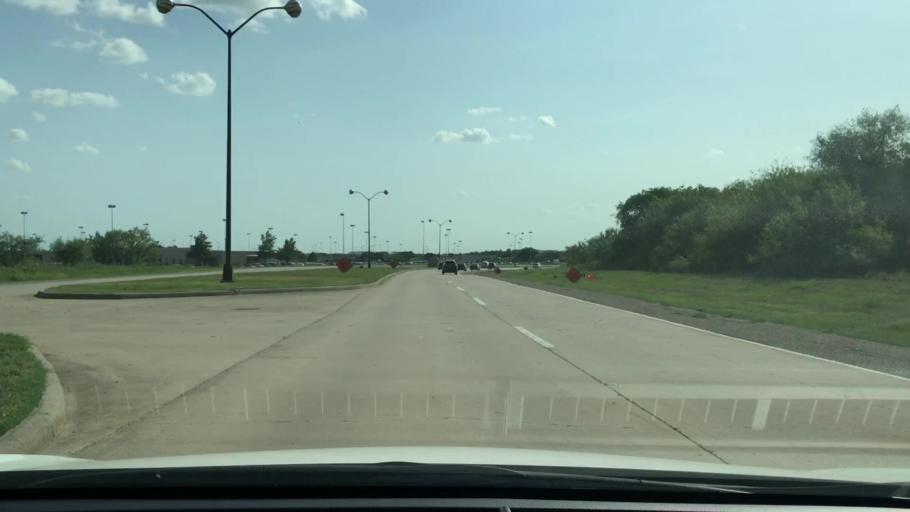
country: US
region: Texas
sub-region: Tarrant County
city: Euless
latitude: 32.8639
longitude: -97.0239
